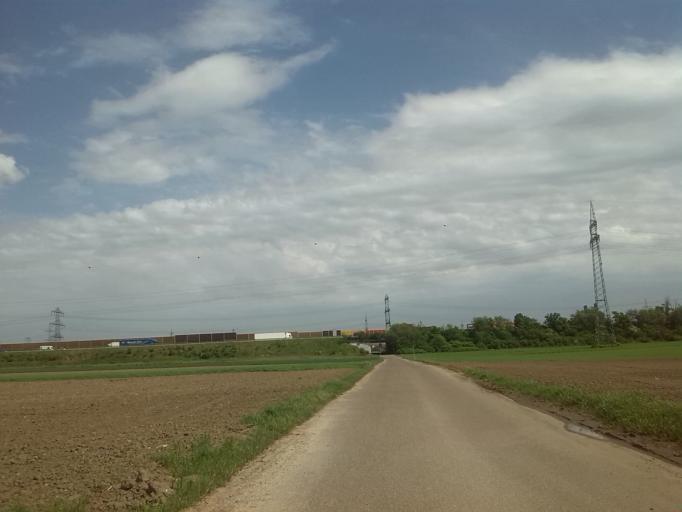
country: DE
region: Baden-Wuerttemberg
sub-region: Karlsruhe Region
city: Ilvesheim
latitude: 49.4652
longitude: 8.5354
